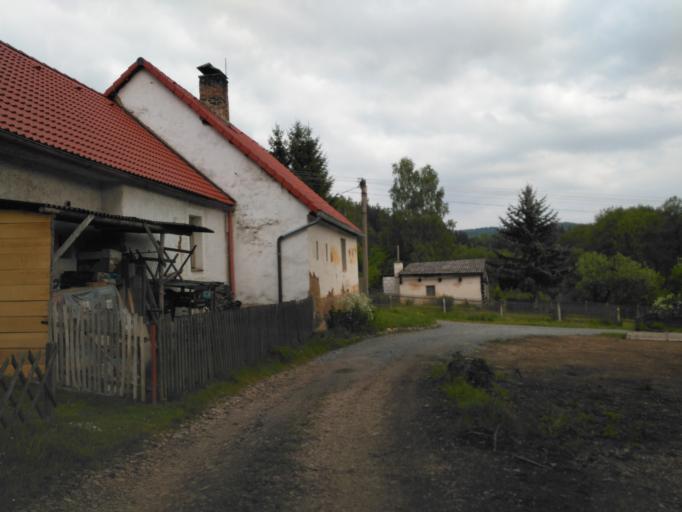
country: CZ
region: Plzensky
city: Zbiroh
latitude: 49.8579
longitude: 13.7286
